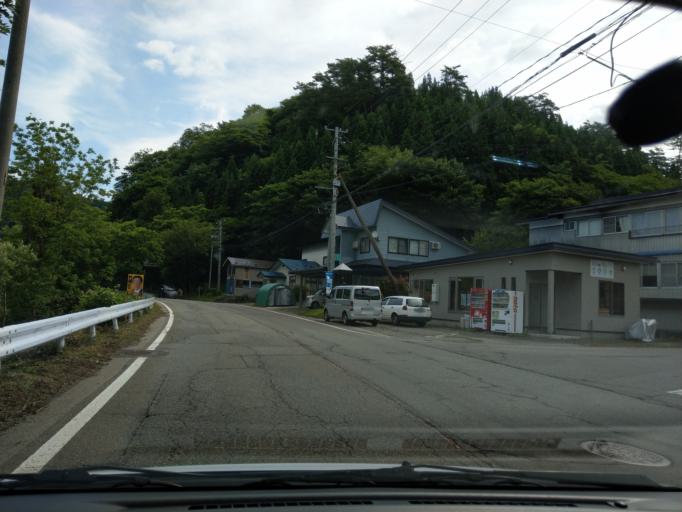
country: JP
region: Akita
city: Kakunodatemachi
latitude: 39.7468
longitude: 140.5986
